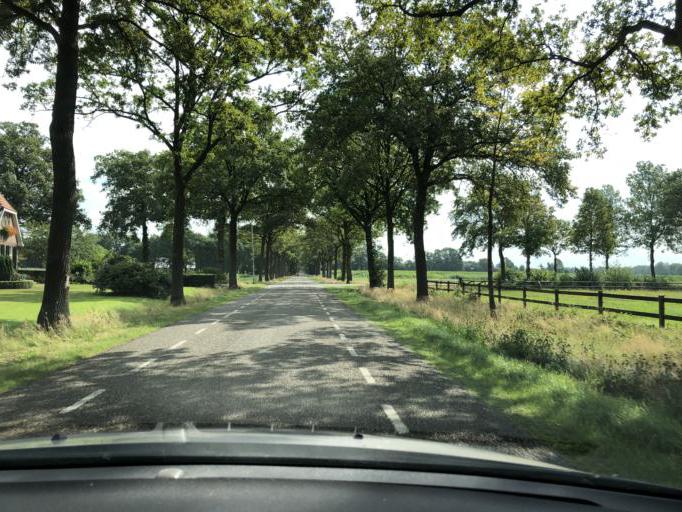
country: NL
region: Overijssel
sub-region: Gemeente Dalfsen
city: Dalfsen
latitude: 52.5767
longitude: 6.3139
